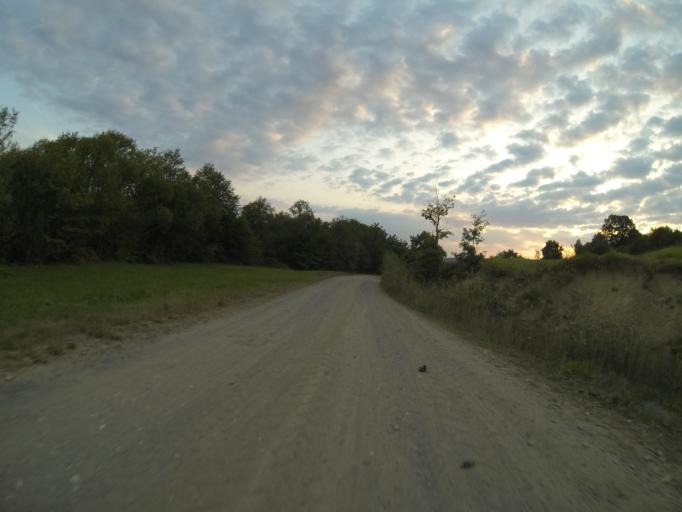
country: RO
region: Brasov
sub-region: Comuna Sinca Noua
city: Sinca Noua
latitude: 45.7132
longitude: 25.2568
